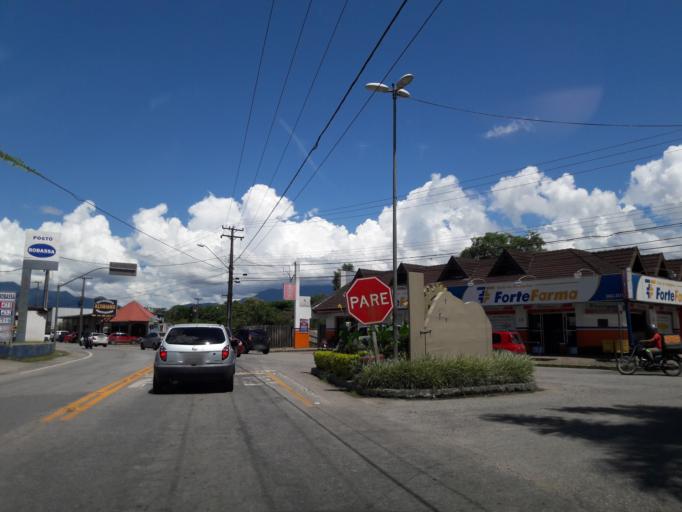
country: BR
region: Parana
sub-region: Antonina
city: Antonina
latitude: -25.4819
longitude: -48.8295
